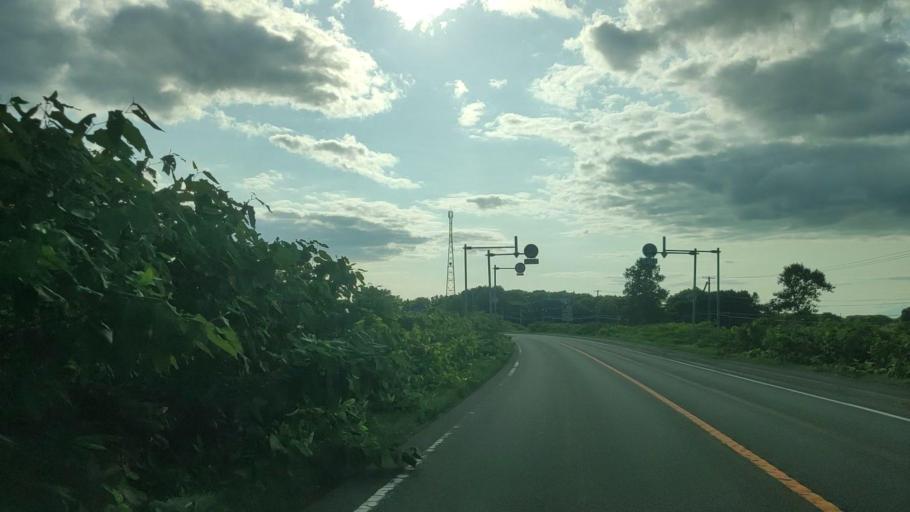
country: JP
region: Hokkaido
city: Makubetsu
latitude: 44.8999
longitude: 141.9363
